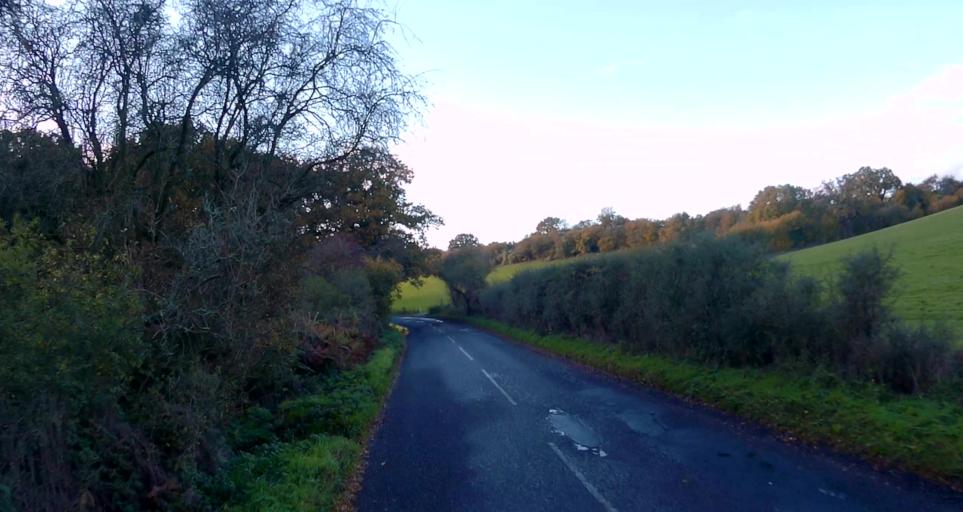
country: GB
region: England
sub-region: Hampshire
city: Basingstoke
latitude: 51.1912
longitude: -1.0809
